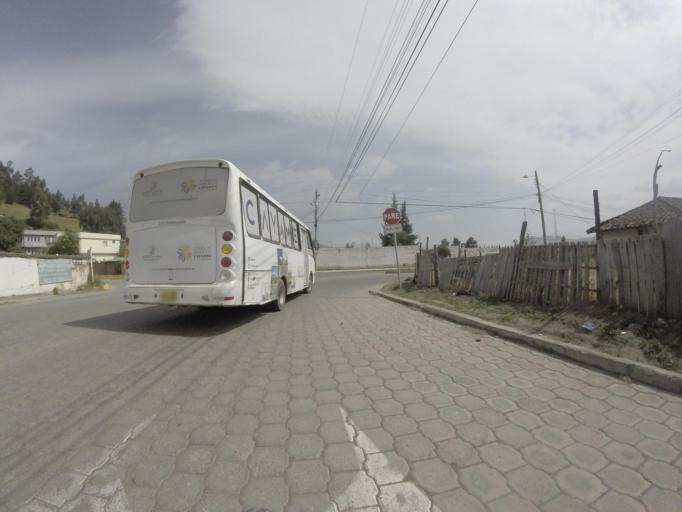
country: EC
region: Pichincha
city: Cayambe
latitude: 0.1491
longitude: -78.0711
